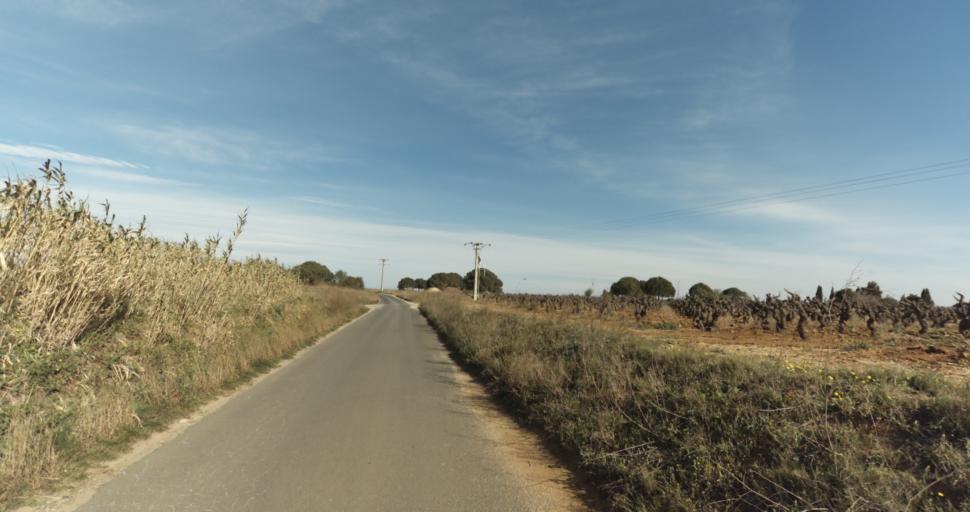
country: FR
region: Languedoc-Roussillon
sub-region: Departement de l'Herault
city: Marseillan
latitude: 43.3445
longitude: 3.5084
